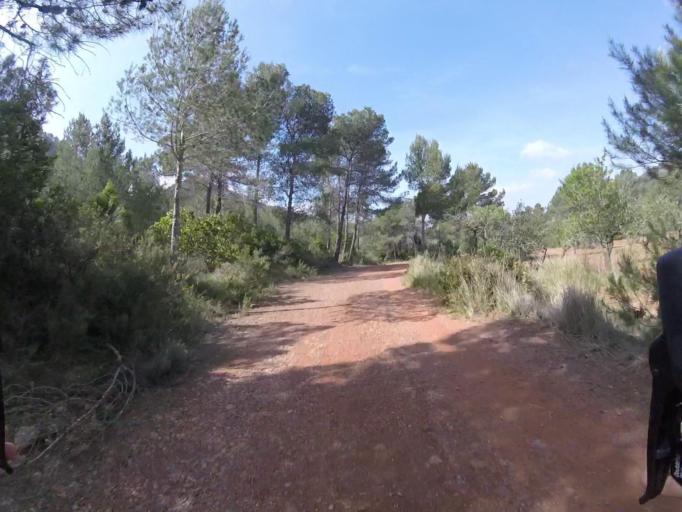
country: ES
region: Valencia
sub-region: Provincia de Castello
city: Benicassim
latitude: 40.0982
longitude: 0.0370
